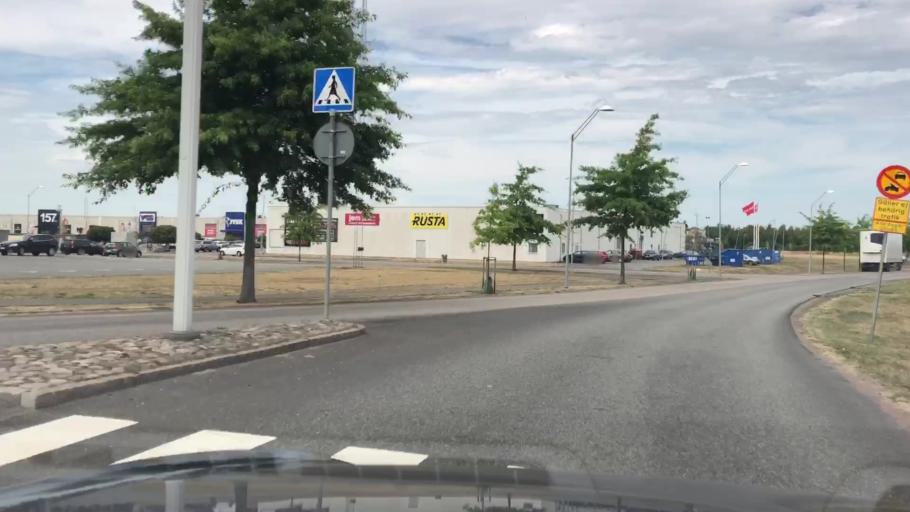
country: SE
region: Skane
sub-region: Kristianstads Kommun
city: Kristianstad
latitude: 56.0223
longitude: 14.1202
